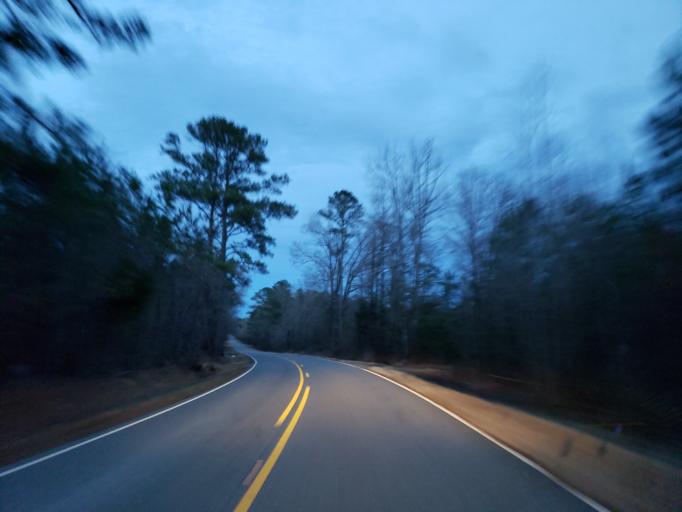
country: US
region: Alabama
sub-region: Greene County
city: Eutaw
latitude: 32.8876
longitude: -88.0457
